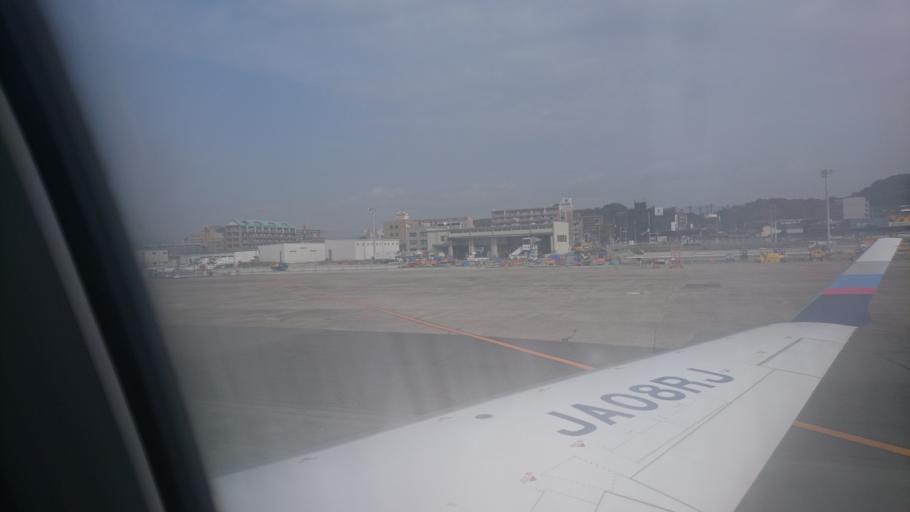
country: JP
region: Fukuoka
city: Fukuoka-shi
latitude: 33.5862
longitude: 130.4528
